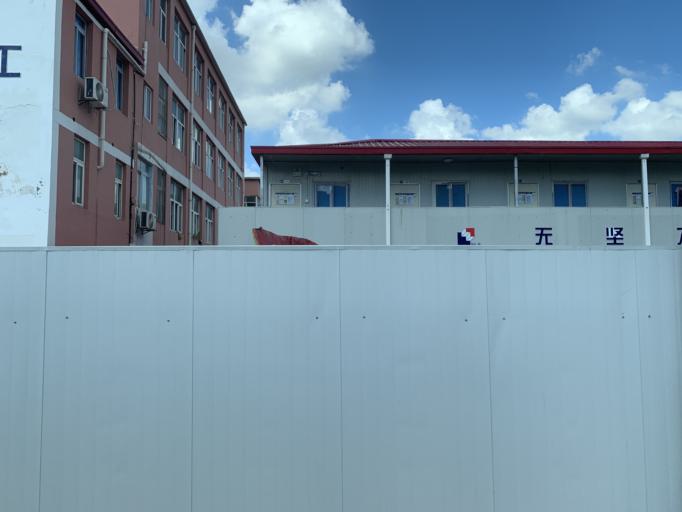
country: CN
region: Shanghai Shi
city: Pudong
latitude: 31.2434
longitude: 121.5375
